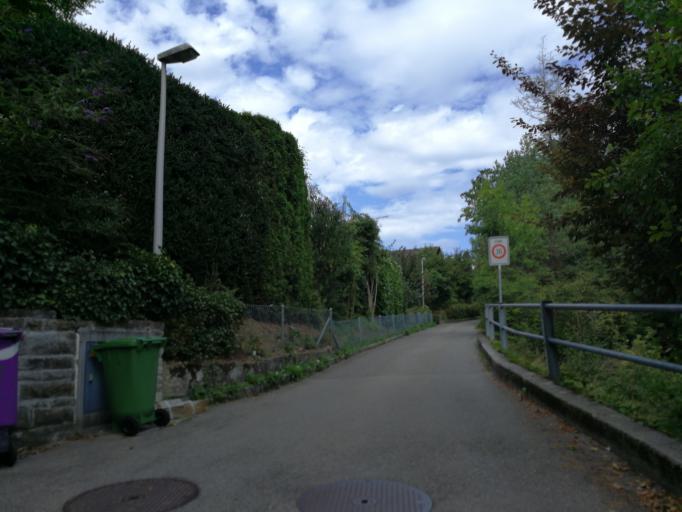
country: CH
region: Zurich
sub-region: Bezirk Meilen
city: Feldmeilen
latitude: 47.2837
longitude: 8.6249
